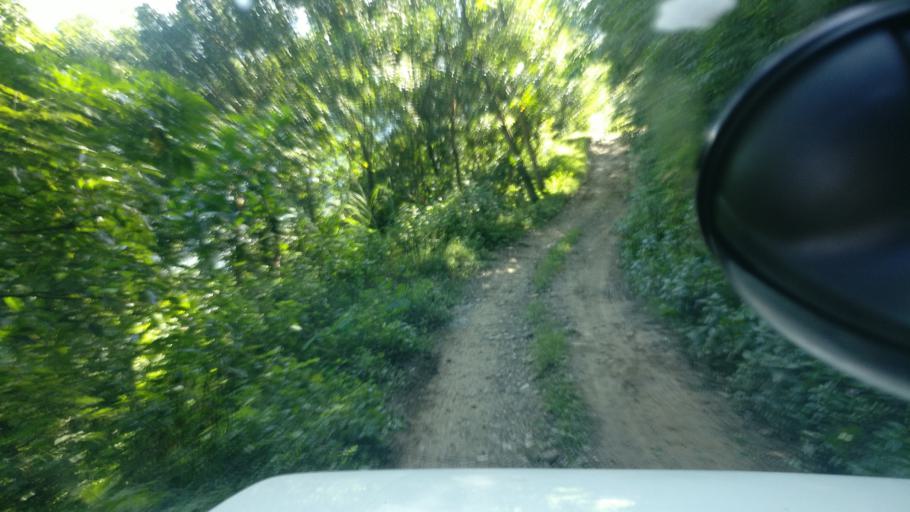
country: NP
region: Western Region
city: Baglung
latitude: 28.1315
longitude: 83.6609
